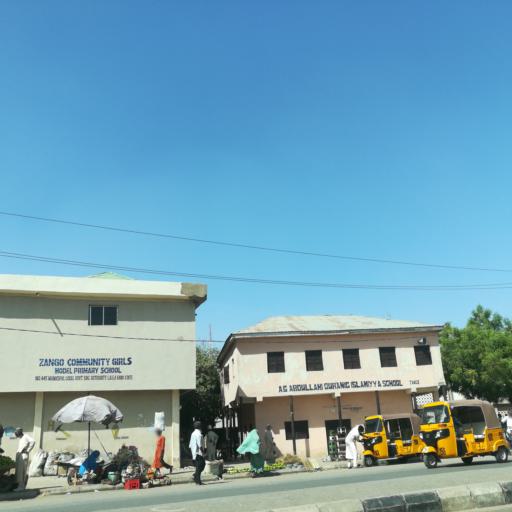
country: NG
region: Kano
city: Kano
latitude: 12.0000
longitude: 8.5252
